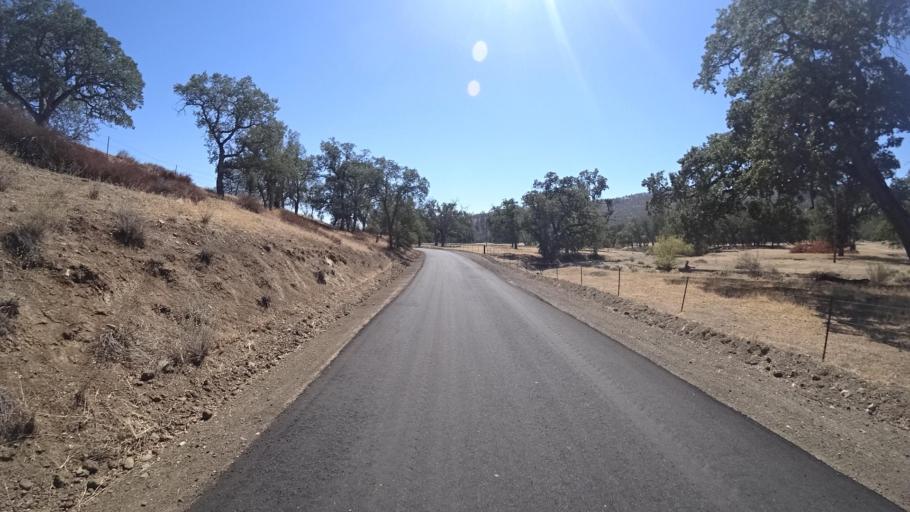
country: US
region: California
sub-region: Fresno County
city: Coalinga
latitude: 35.9347
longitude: -120.4591
